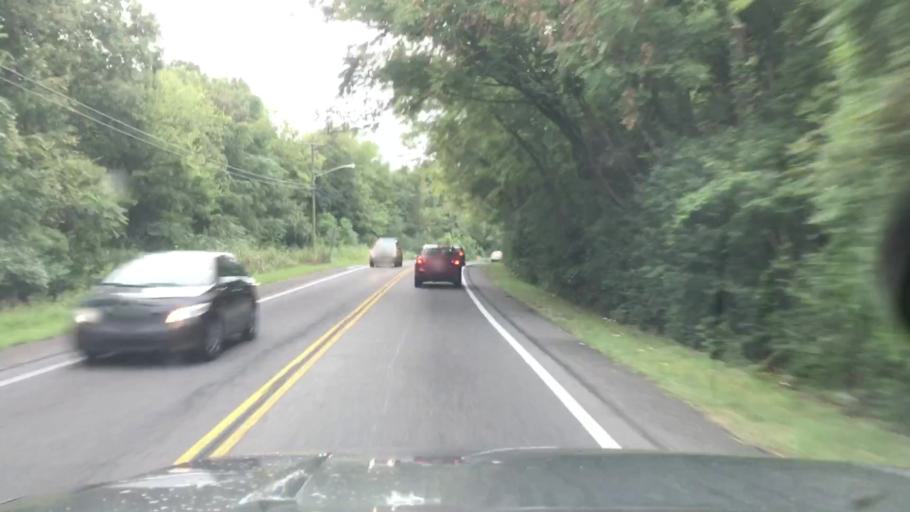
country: US
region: Tennessee
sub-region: Davidson County
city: Lakewood
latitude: 36.1393
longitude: -86.6284
